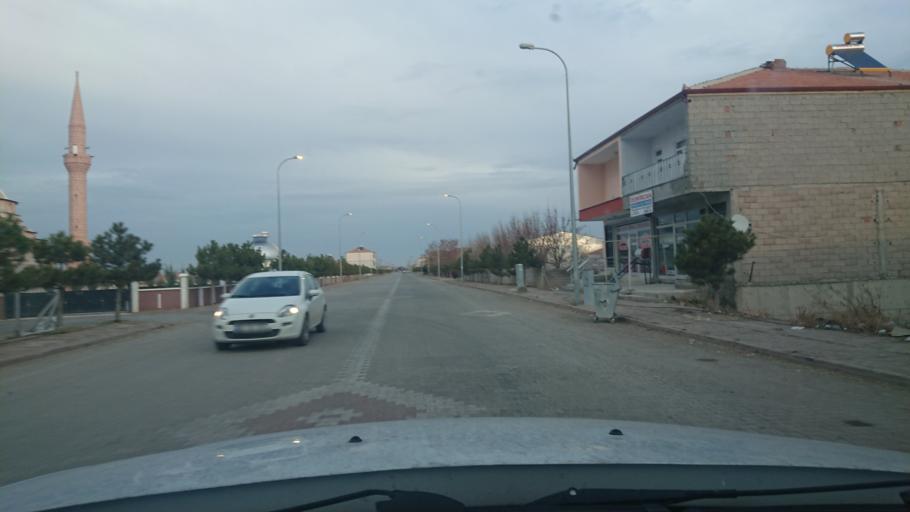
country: TR
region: Aksaray
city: Yesilova
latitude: 38.3327
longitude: 33.7519
